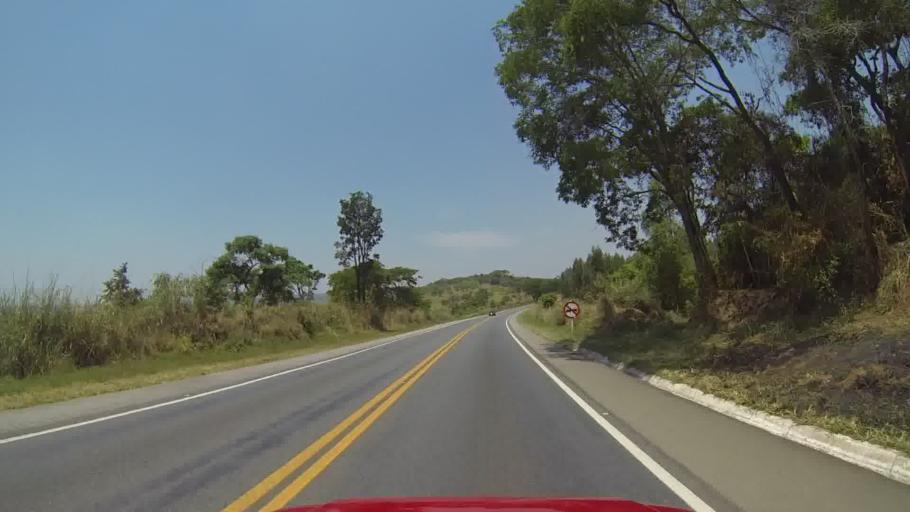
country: BR
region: Minas Gerais
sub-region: Itapecerica
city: Itapecerica
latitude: -20.3159
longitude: -45.2209
